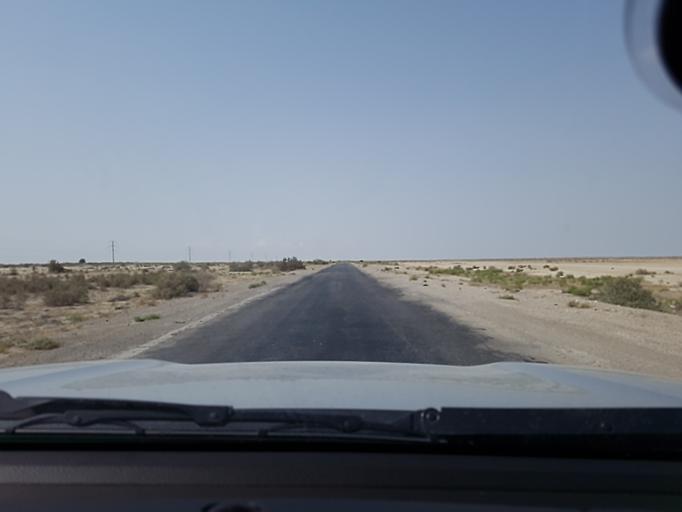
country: TM
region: Balkan
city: Gumdag
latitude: 38.7816
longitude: 54.5933
